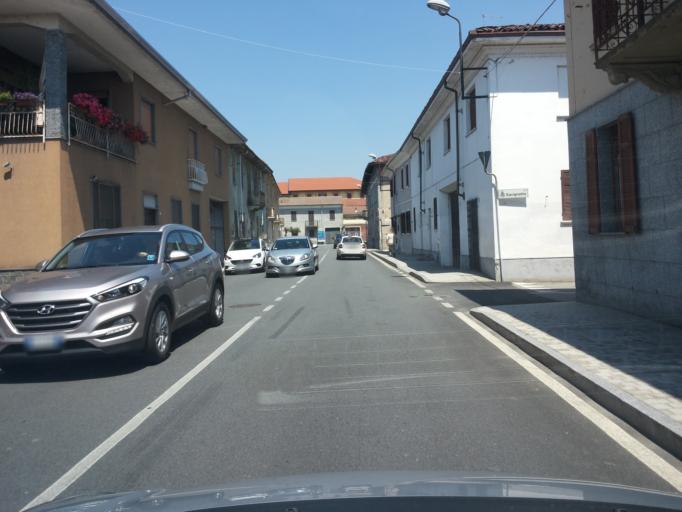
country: IT
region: Piedmont
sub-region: Provincia di Novara
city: Casalvolone
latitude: 45.3986
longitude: 8.4638
